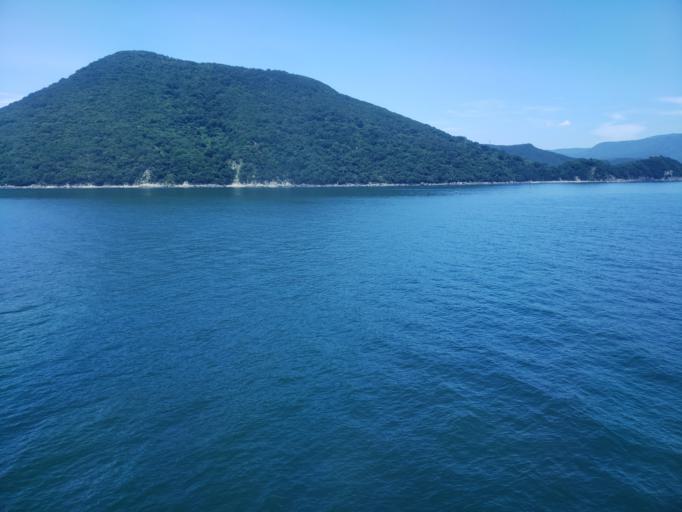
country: JP
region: Kagawa
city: Tonosho
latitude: 34.4100
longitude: 134.2469
